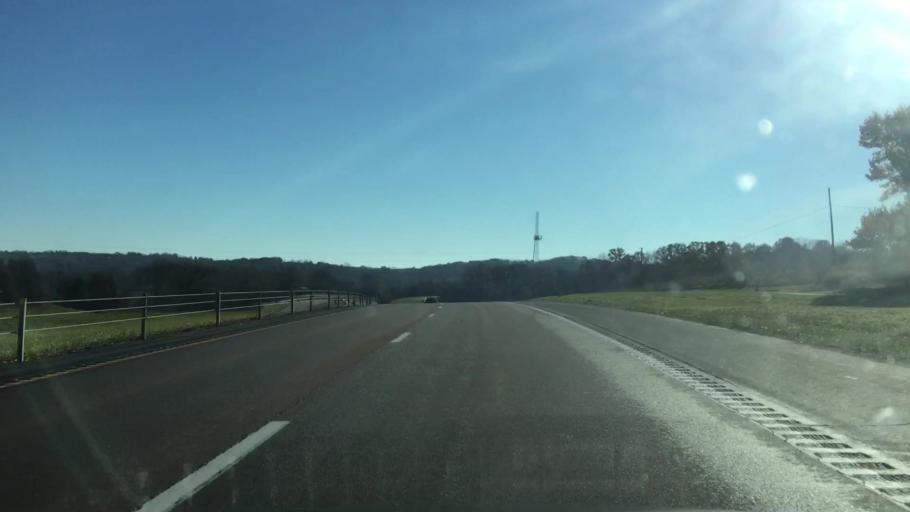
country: US
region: Missouri
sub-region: Cole County
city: Jefferson City
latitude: 38.6528
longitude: -92.2116
